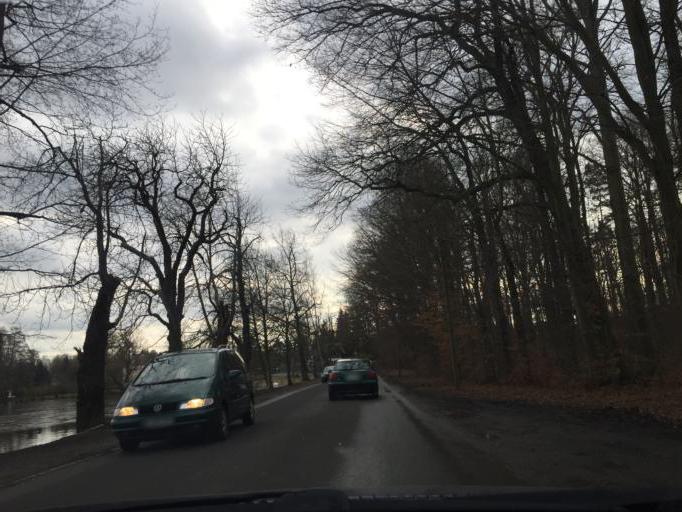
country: DE
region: Saxony
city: Moritzburg
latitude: 51.1679
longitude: 13.6728
